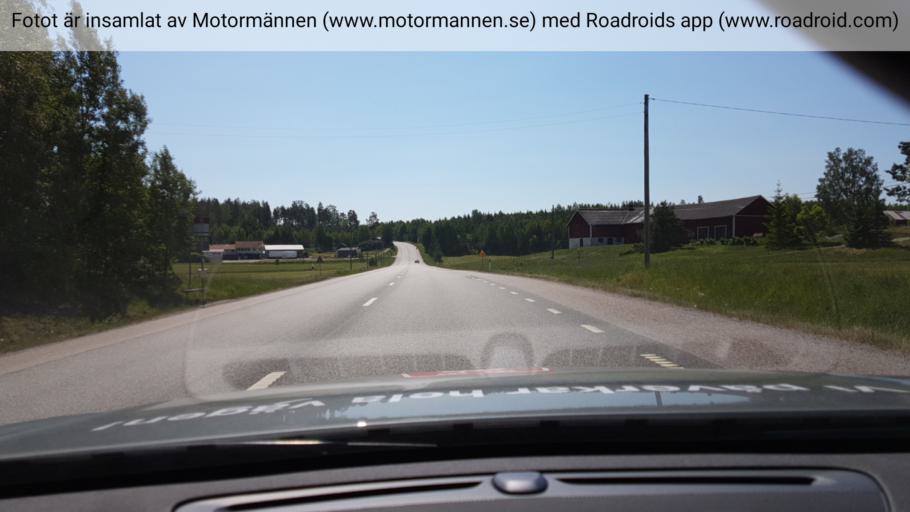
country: SE
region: Stockholm
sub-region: Norrtalje Kommun
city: Rimbo
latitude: 59.6474
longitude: 18.3335
